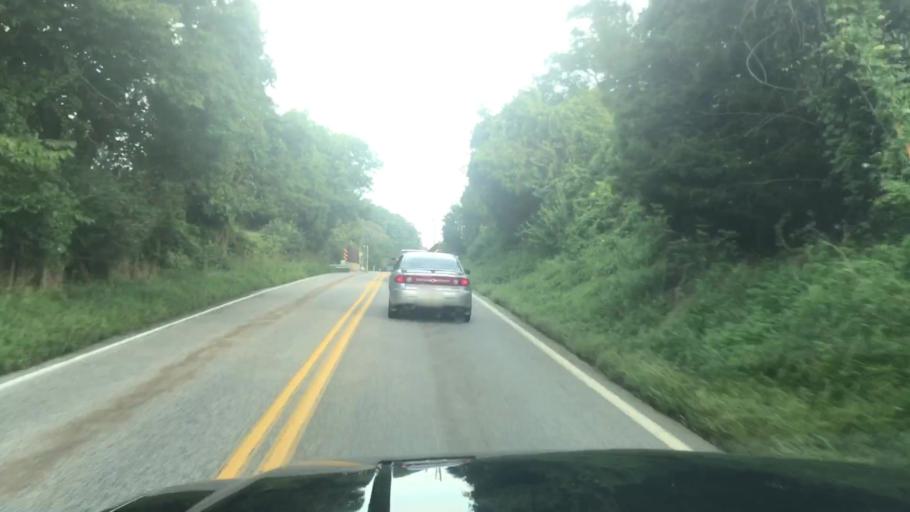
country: US
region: Pennsylvania
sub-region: Cumberland County
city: Shiremanstown
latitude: 40.1993
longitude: -76.9485
